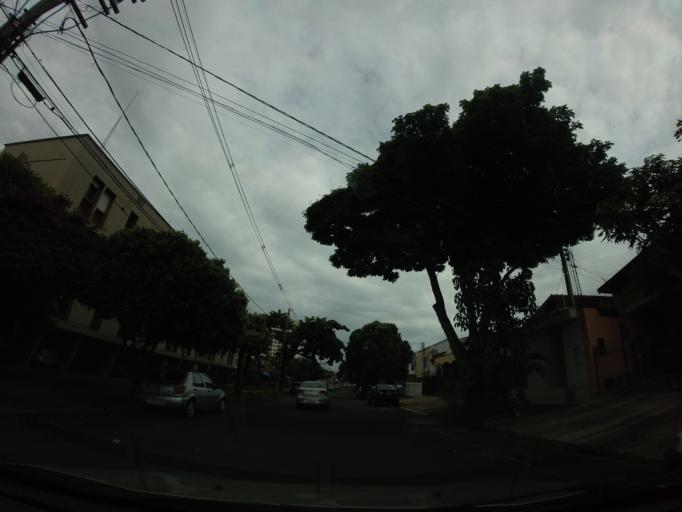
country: BR
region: Sao Paulo
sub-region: Piracicaba
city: Piracicaba
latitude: -22.7091
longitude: -47.6637
